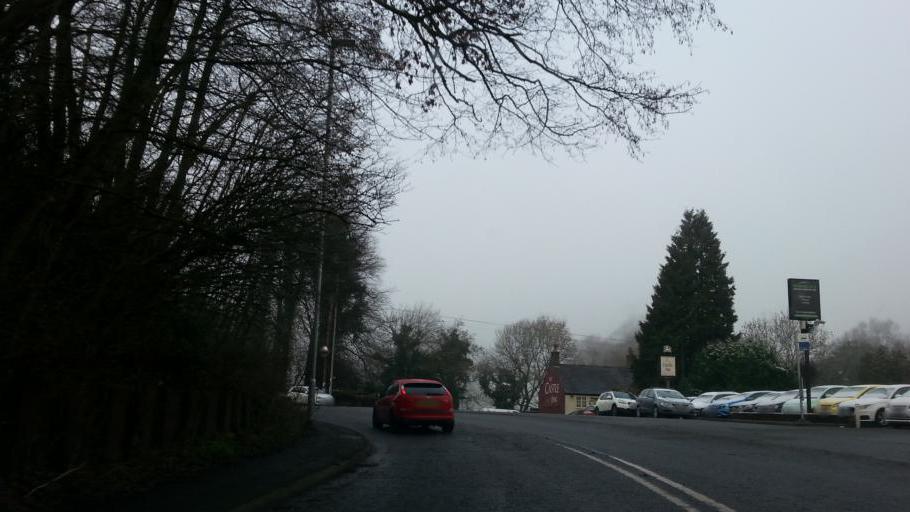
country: GB
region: England
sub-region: Staffordshire
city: Biddulph
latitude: 53.1487
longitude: -2.1753
